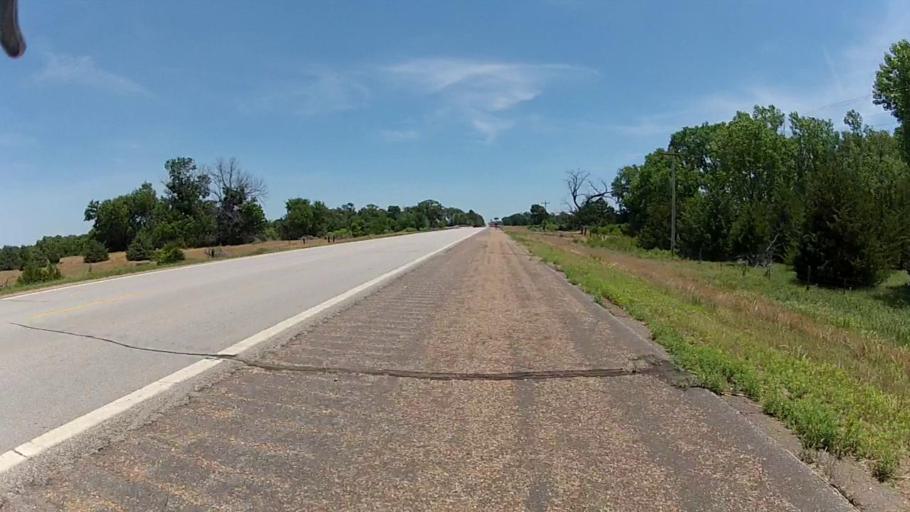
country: US
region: Kansas
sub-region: Barber County
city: Medicine Lodge
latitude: 37.2534
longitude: -98.3315
